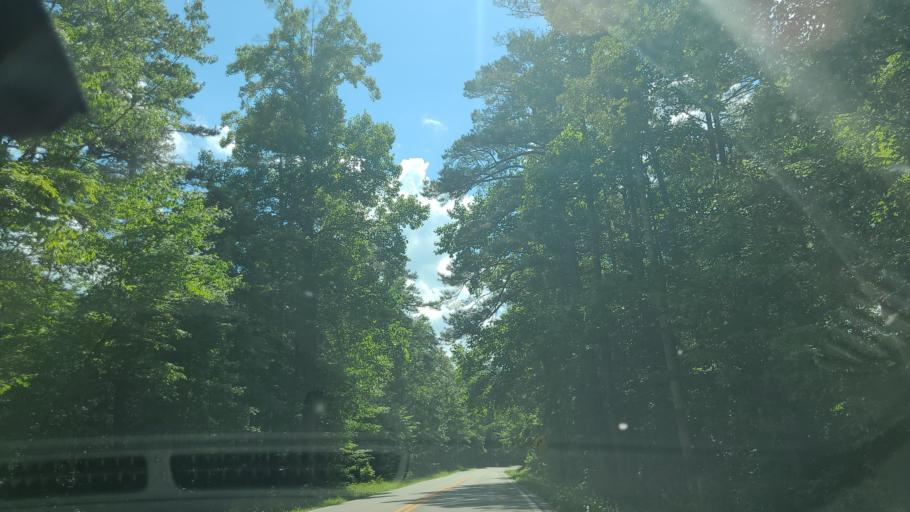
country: US
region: Kentucky
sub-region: Whitley County
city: Williamsburg
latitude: 36.8384
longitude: -84.2685
